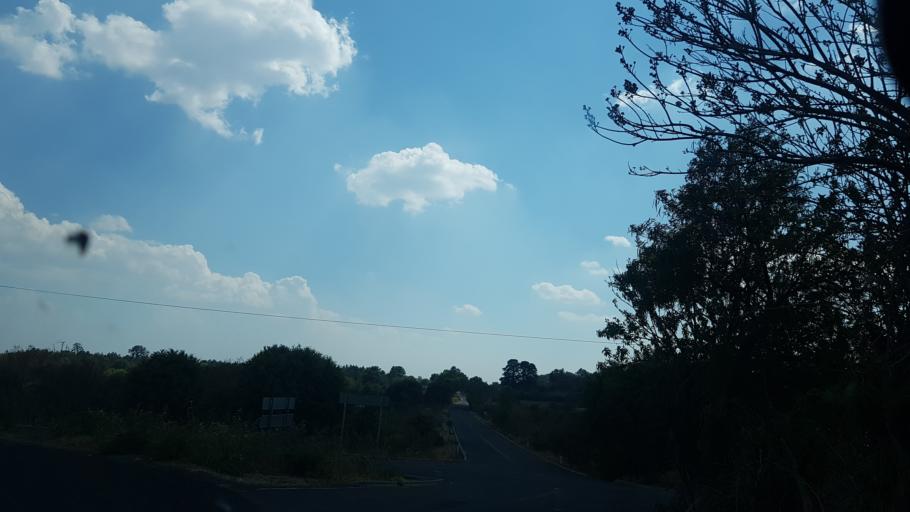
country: MX
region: Puebla
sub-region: Atlixco
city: San Pedro Benito Juarez
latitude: 18.9438
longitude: -98.5355
